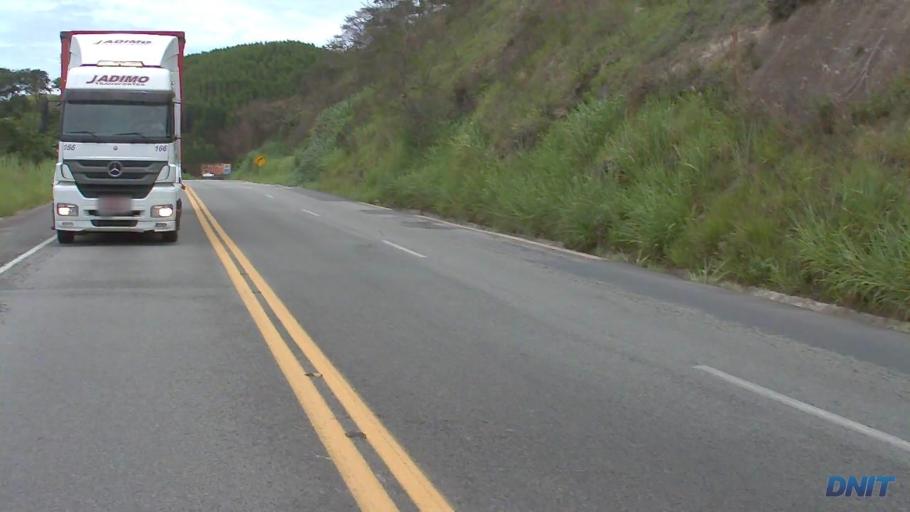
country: BR
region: Minas Gerais
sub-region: Nova Era
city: Nova Era
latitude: -19.6696
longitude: -42.9683
